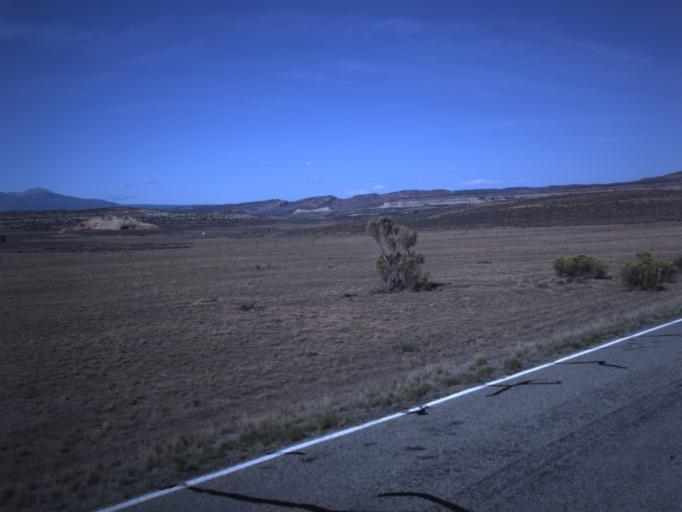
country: US
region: Utah
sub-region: San Juan County
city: Monticello
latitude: 38.0710
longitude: -109.3624
